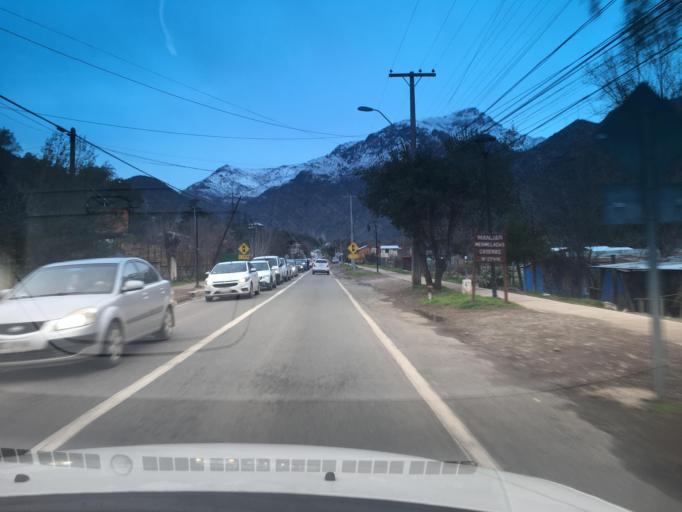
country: CL
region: Santiago Metropolitan
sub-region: Provincia de Cordillera
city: Puente Alto
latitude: -33.6963
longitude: -70.3348
